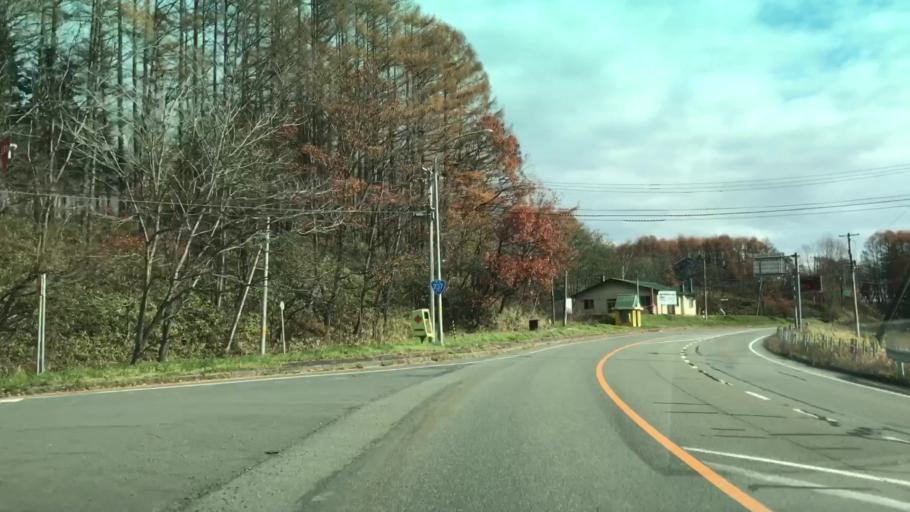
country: JP
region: Hokkaido
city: Shizunai-furukawacho
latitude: 42.7180
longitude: 142.2608
